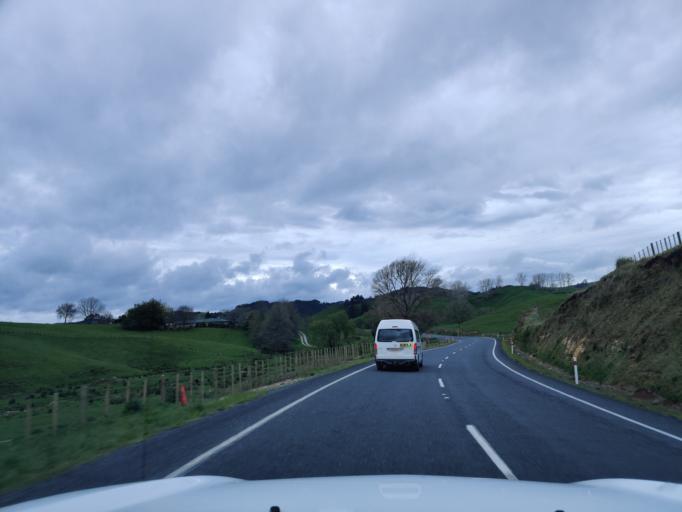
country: NZ
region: Waikato
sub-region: Otorohanga District
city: Otorohanga
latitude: -38.4534
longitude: 175.1639
